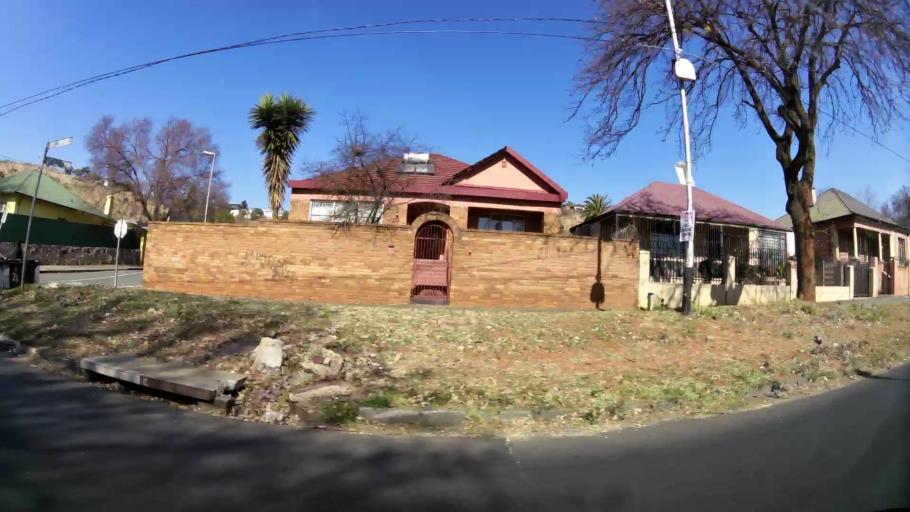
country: ZA
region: Gauteng
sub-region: City of Johannesburg Metropolitan Municipality
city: Johannesburg
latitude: -26.1937
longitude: 28.0786
